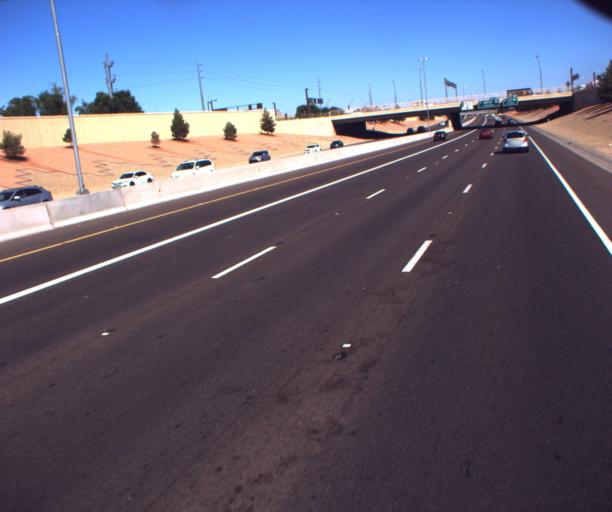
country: US
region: Arizona
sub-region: Maricopa County
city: San Carlos
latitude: 33.3332
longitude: -111.8927
